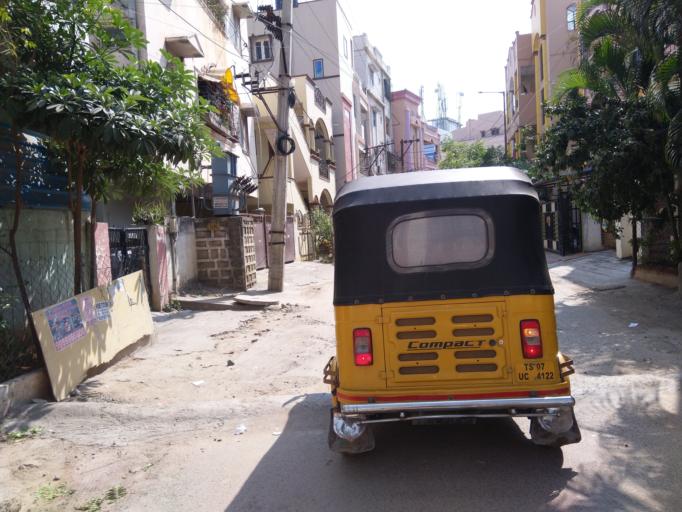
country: IN
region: Telangana
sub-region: Rangareddi
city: Kukatpalli
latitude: 17.4979
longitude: 78.4073
